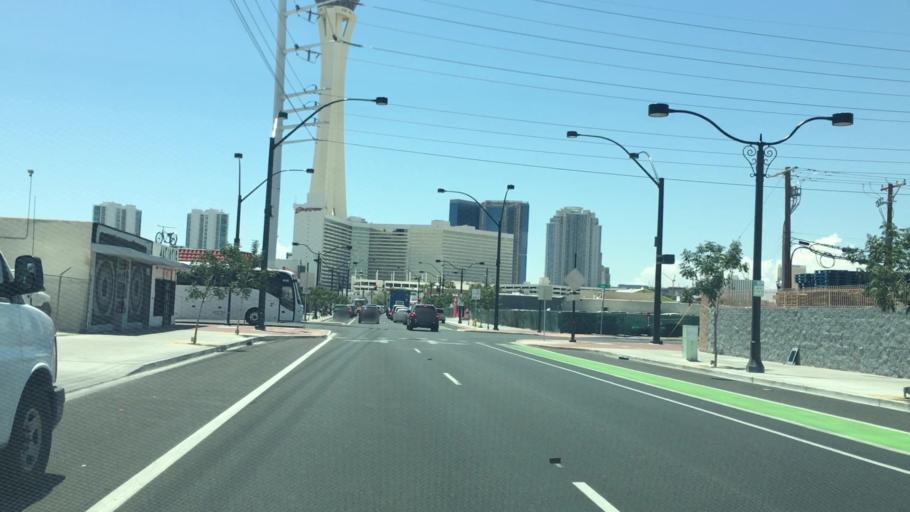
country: US
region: Nevada
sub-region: Clark County
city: Las Vegas
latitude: 36.1541
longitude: -115.1553
